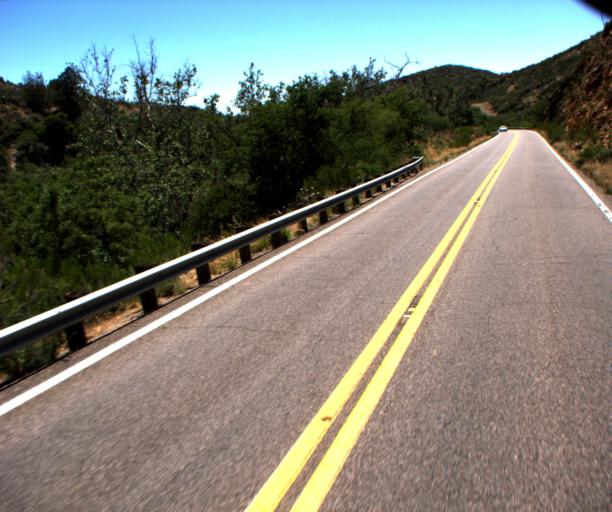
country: US
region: Arizona
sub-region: Gila County
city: Globe
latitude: 33.2176
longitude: -110.7947
